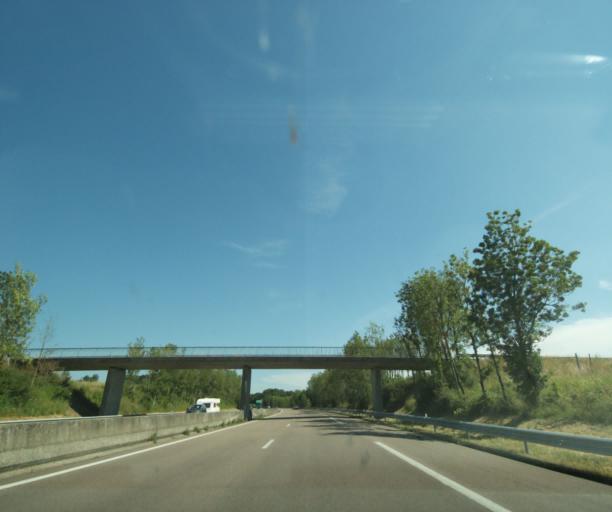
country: FR
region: Lorraine
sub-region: Departement des Vosges
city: Chatenois
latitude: 48.3965
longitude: 5.8808
